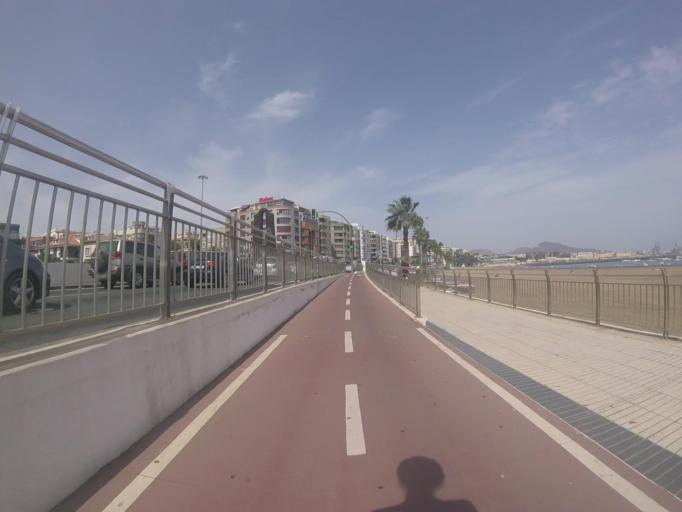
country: ES
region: Canary Islands
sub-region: Provincia de Las Palmas
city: Las Palmas de Gran Canaria
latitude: 28.1288
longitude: -15.4295
